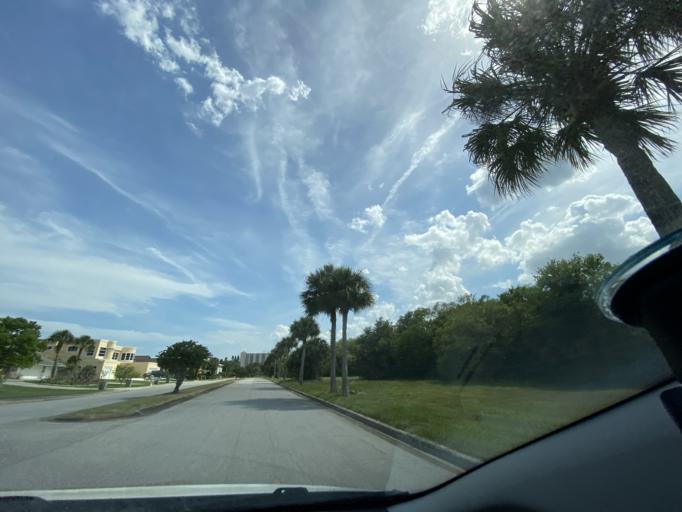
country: US
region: Florida
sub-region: Volusia County
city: South Daytona
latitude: 29.1640
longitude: -80.9966
